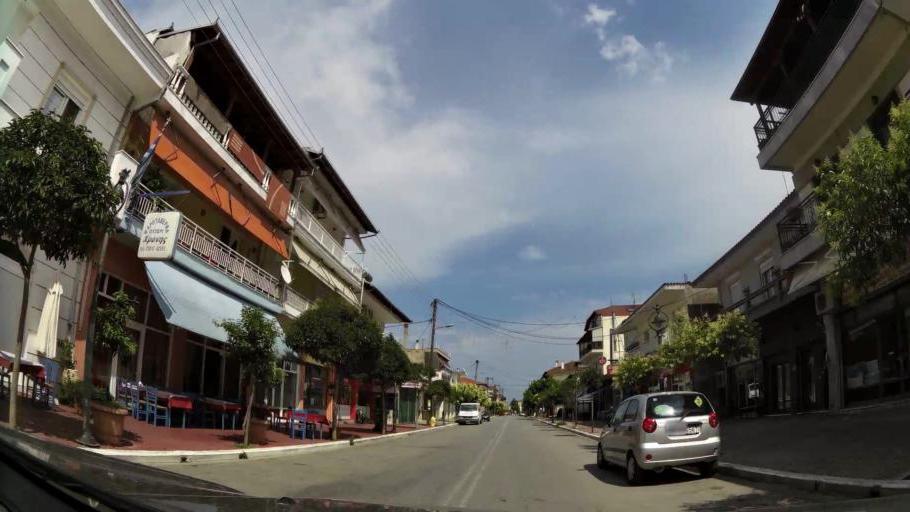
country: GR
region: Central Macedonia
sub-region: Nomos Pierias
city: Korinos
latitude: 40.3159
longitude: 22.5810
